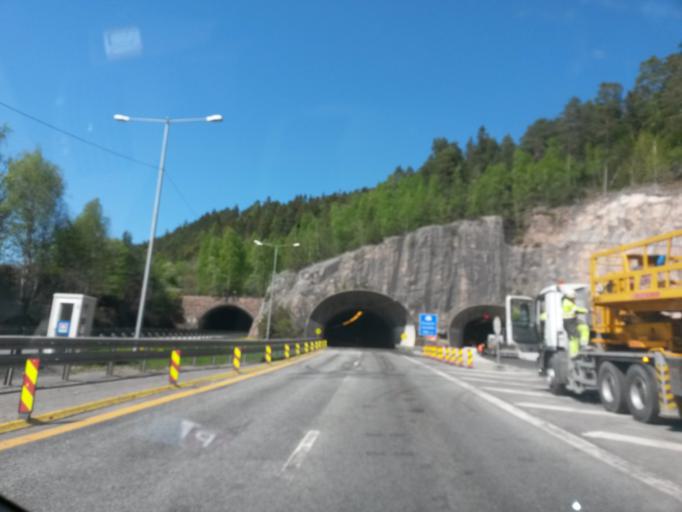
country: NO
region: Buskerud
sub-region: Lier
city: Tranby
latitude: 59.7904
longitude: 10.2725
